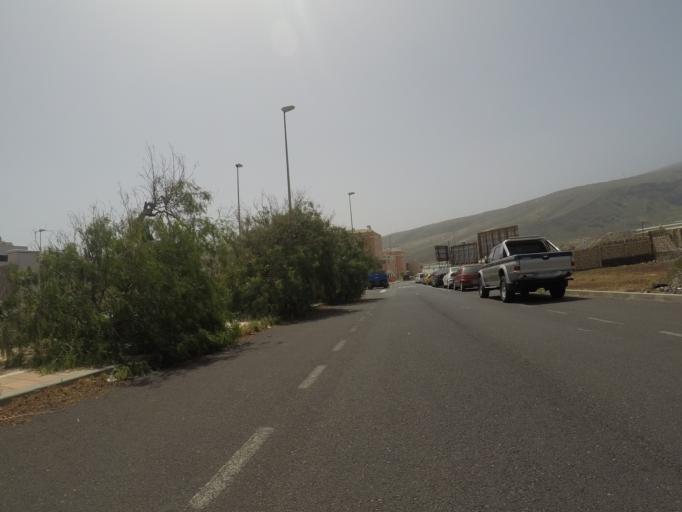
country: ES
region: Canary Islands
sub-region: Provincia de Santa Cruz de Tenerife
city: Candelaria
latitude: 28.2976
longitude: -16.3751
